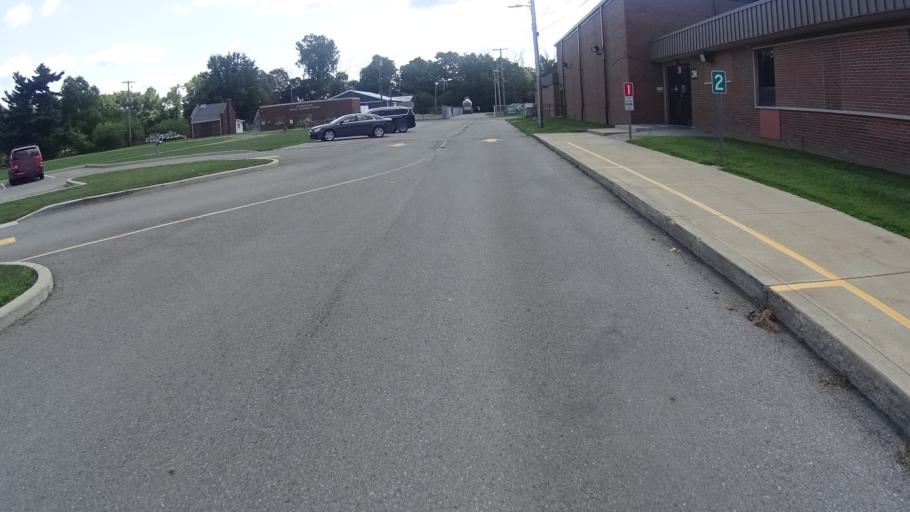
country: US
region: Indiana
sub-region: Madison County
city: Pendleton
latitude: 39.9991
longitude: -85.7405
